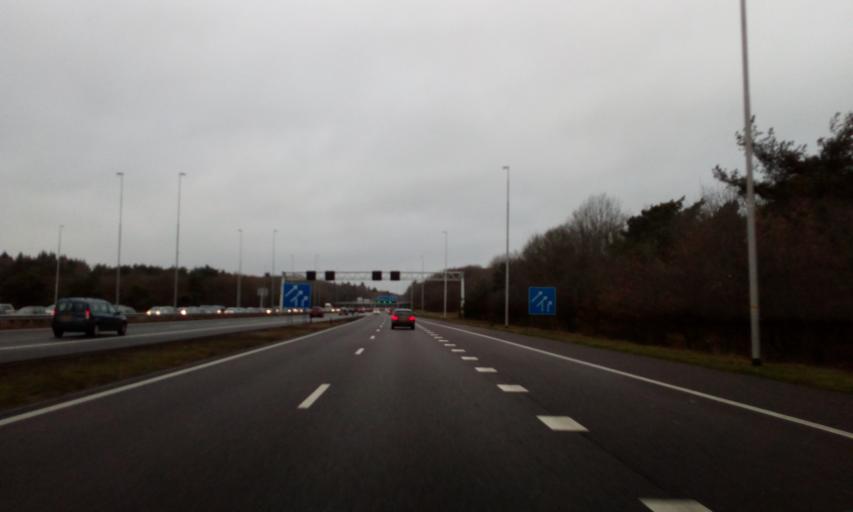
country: NL
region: North Holland
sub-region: Gemeente Laren
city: Laren
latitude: 52.2397
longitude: 5.2267
